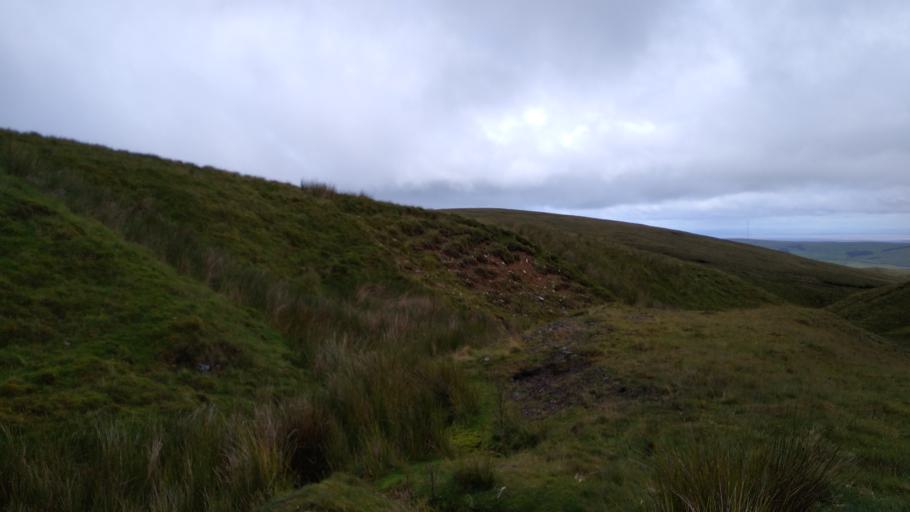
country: GB
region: England
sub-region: Cumbria
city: Keswick
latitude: 54.7075
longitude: -3.0681
